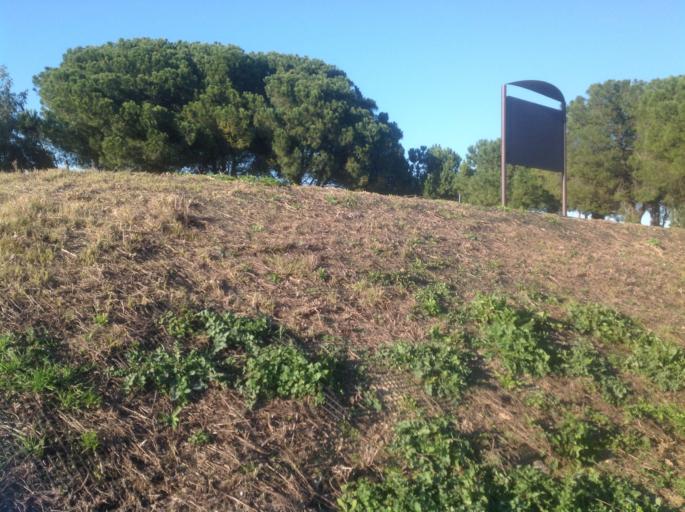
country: IT
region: Calabria
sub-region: Provincia di Cosenza
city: Sibari
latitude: 39.7161
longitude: 16.4913
